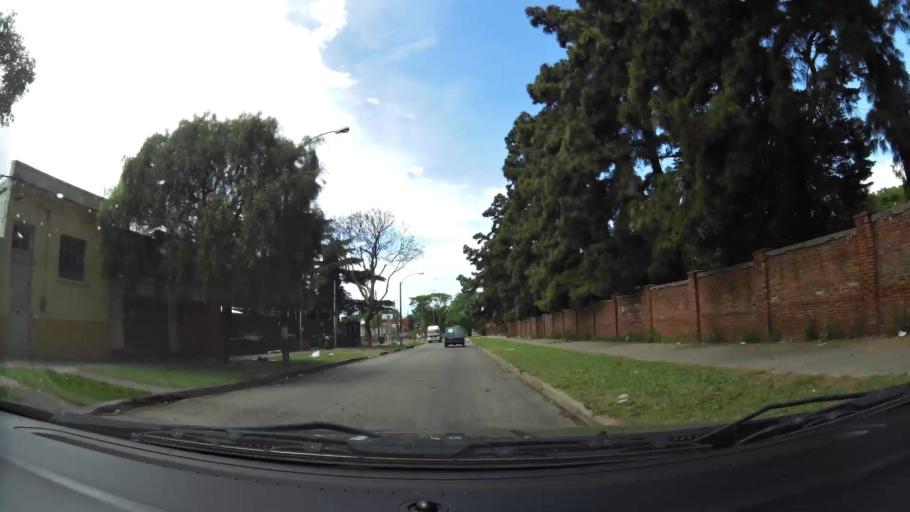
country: UY
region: Montevideo
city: Montevideo
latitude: -34.8766
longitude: -56.1359
